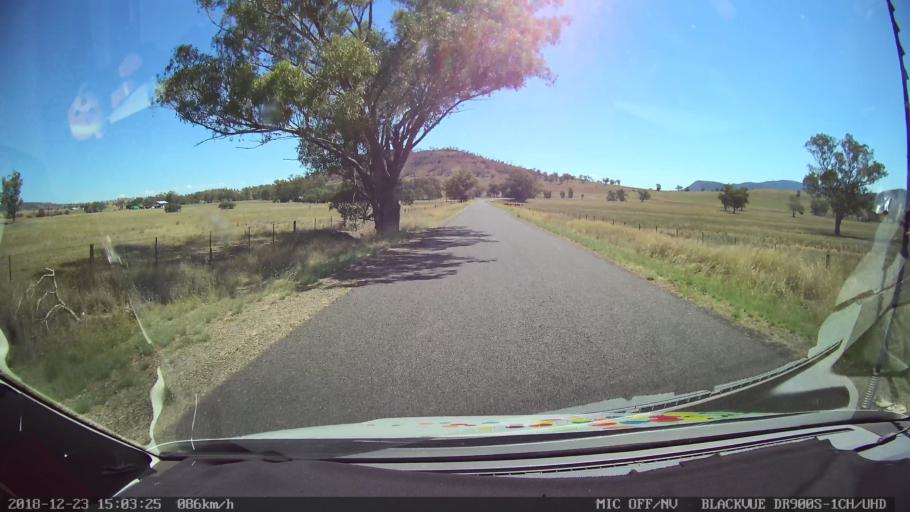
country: AU
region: New South Wales
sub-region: Tamworth Municipality
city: Manilla
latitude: -30.7384
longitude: 150.7652
